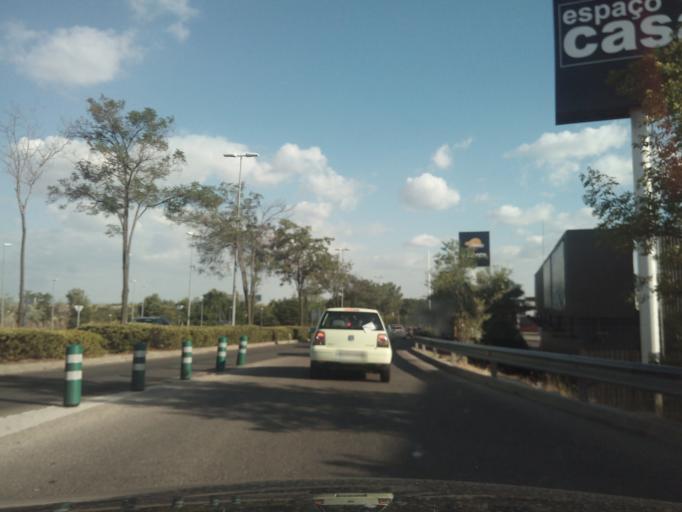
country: ES
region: Madrid
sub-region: Provincia de Madrid
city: San Sebastian de los Reyes
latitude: 40.5454
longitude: -3.6099
